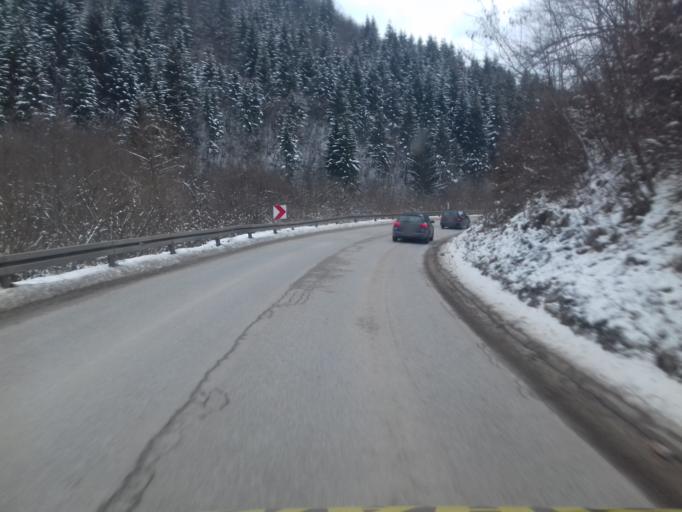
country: BA
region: Republika Srpska
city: Pale
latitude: 43.8652
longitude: 18.5501
